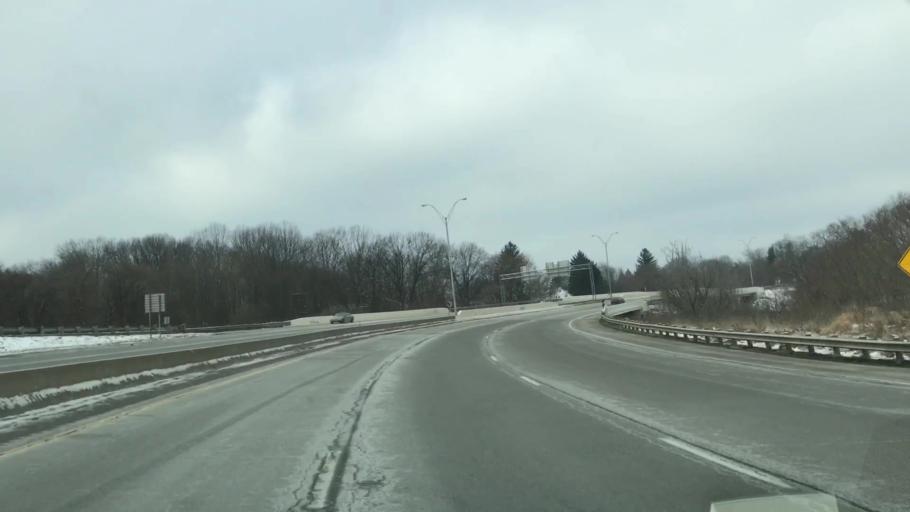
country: US
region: Ohio
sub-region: Mahoning County
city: Youngstown
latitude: 41.0818
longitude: -80.6470
